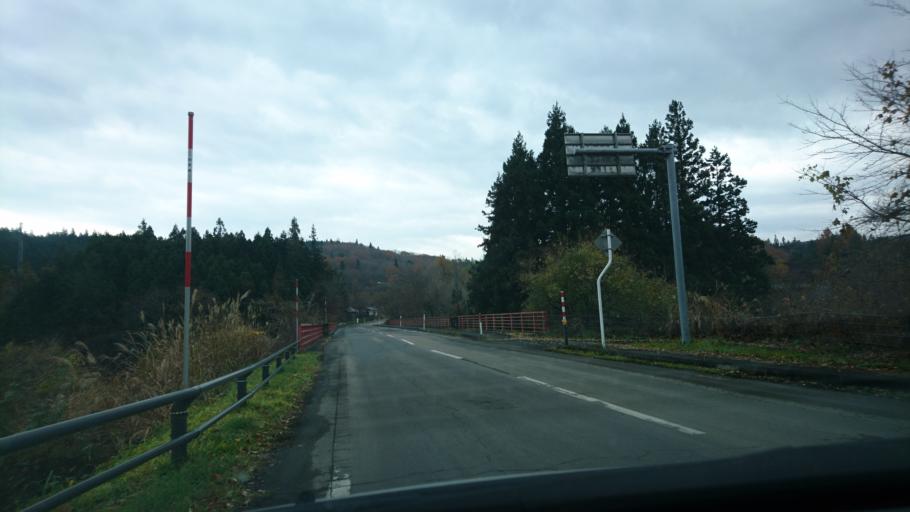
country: JP
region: Iwate
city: Ichinoseki
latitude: 38.9739
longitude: 140.9416
